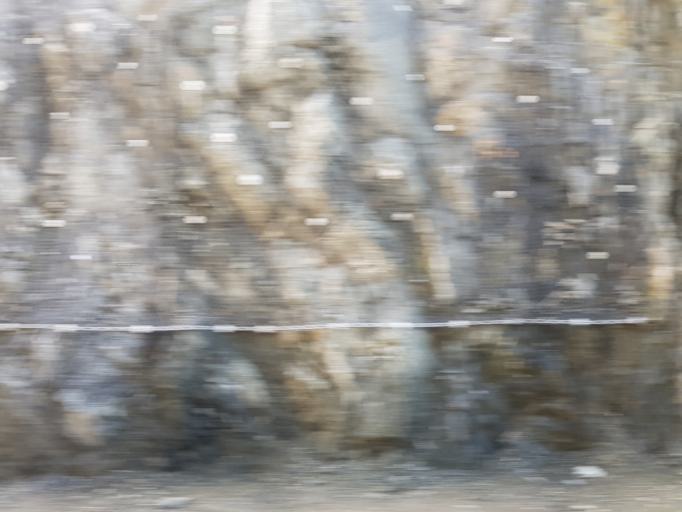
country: NO
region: Sor-Trondelag
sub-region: Trondheim
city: Trondheim
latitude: 63.6728
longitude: 10.2442
